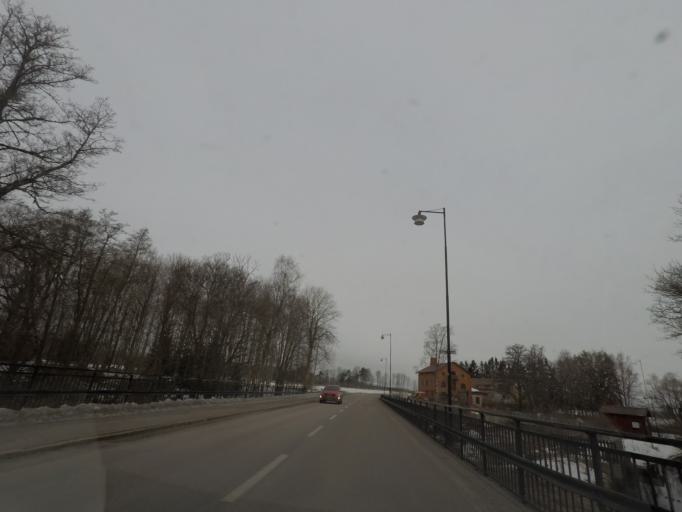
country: SE
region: Vaestmanland
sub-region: Vasteras
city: Skultuna
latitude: 59.7229
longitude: 16.4241
